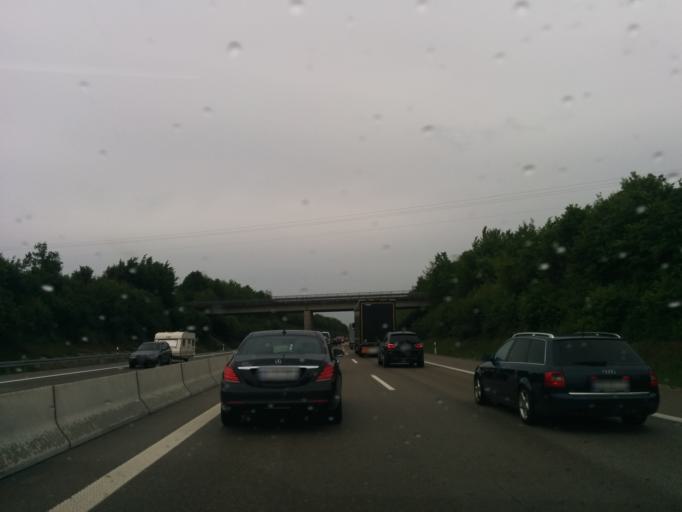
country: DE
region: Bavaria
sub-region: Regierungsbezirk Unterfranken
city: Martinsheim
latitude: 49.6175
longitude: 10.1728
